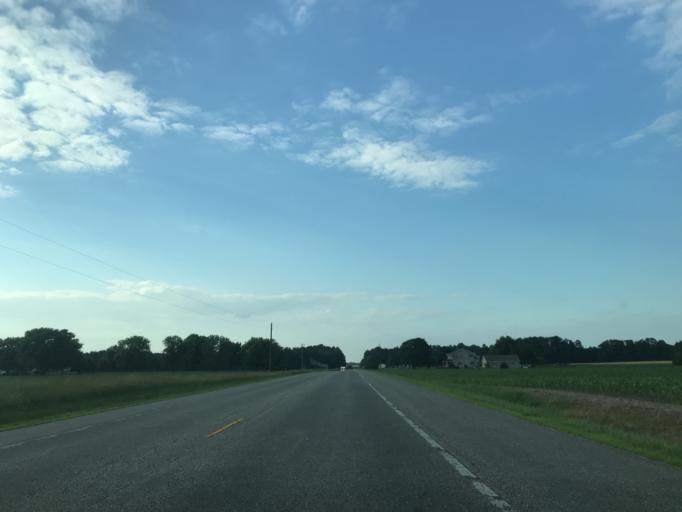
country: US
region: Maryland
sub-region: Caroline County
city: Federalsburg
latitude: 38.7832
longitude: -75.7875
